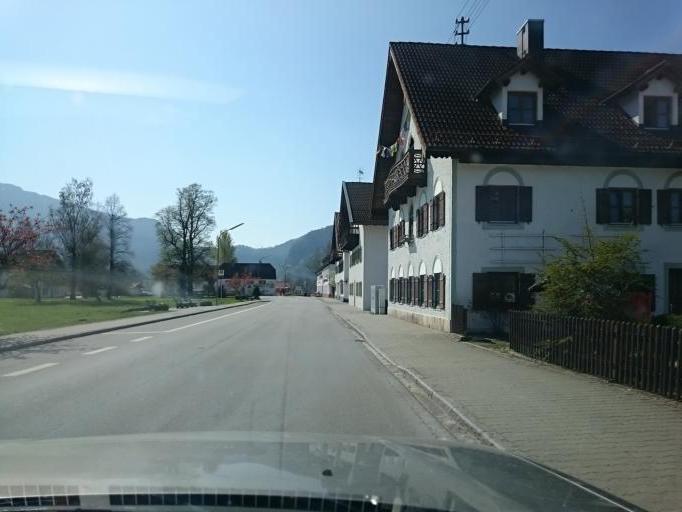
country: DE
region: Bavaria
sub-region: Upper Bavaria
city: Schlehdorf
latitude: 47.6571
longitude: 11.3156
